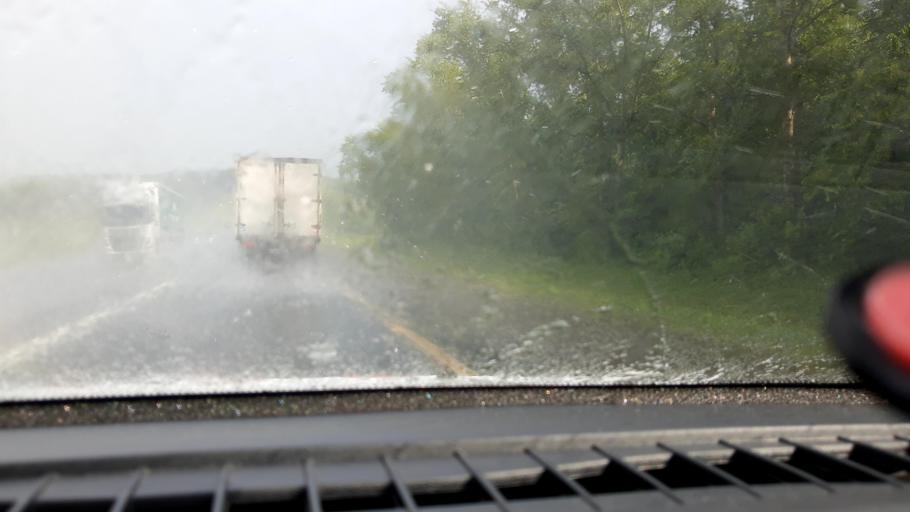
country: RU
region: Nizjnij Novgorod
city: Pamyat' Parizhskoy Kommuny
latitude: 56.0494
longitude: 44.4156
